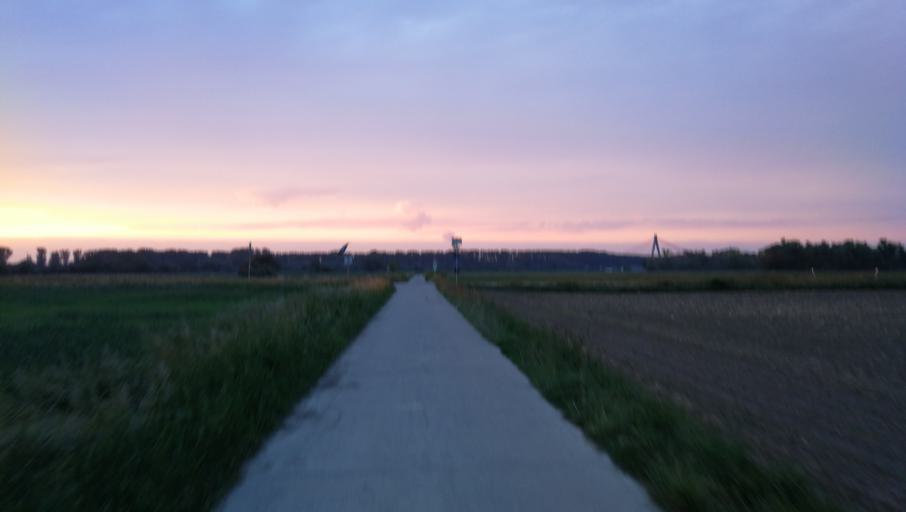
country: DE
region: Baden-Wuerttemberg
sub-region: Karlsruhe Region
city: Altlussheim
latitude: 49.3239
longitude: 8.4725
